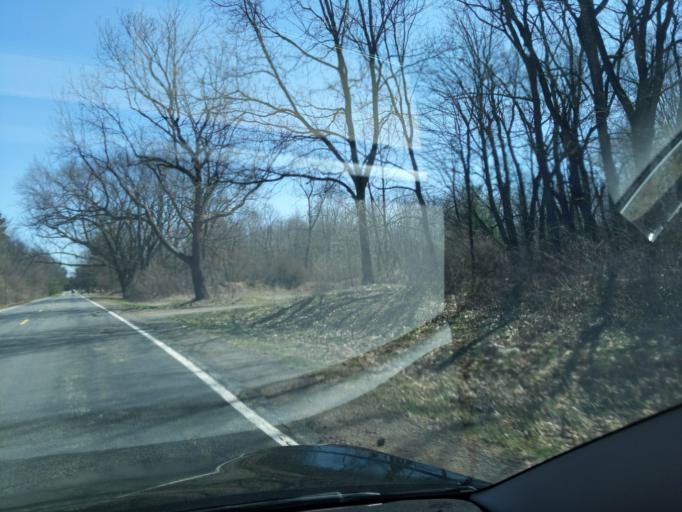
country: US
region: Michigan
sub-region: Ingham County
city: Mason
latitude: 42.5377
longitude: -84.3495
